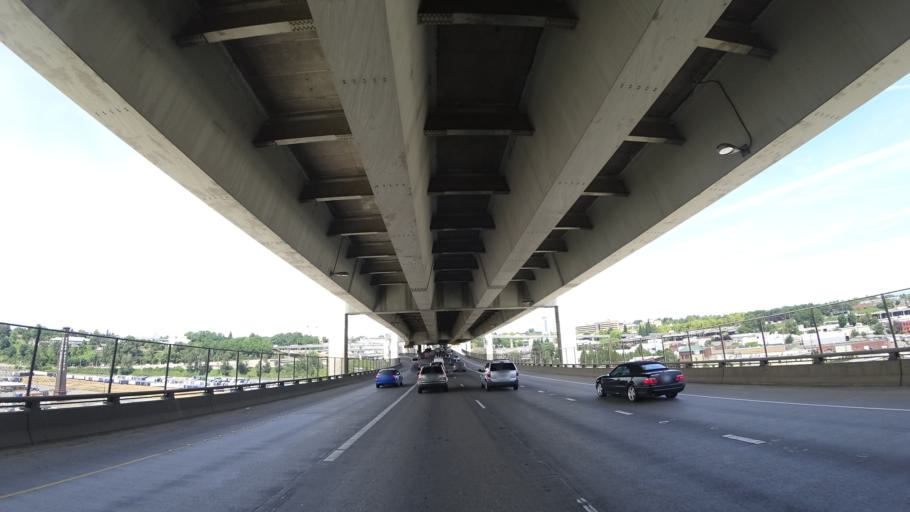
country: US
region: Oregon
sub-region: Multnomah County
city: Portland
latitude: 45.5420
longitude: -122.6801
